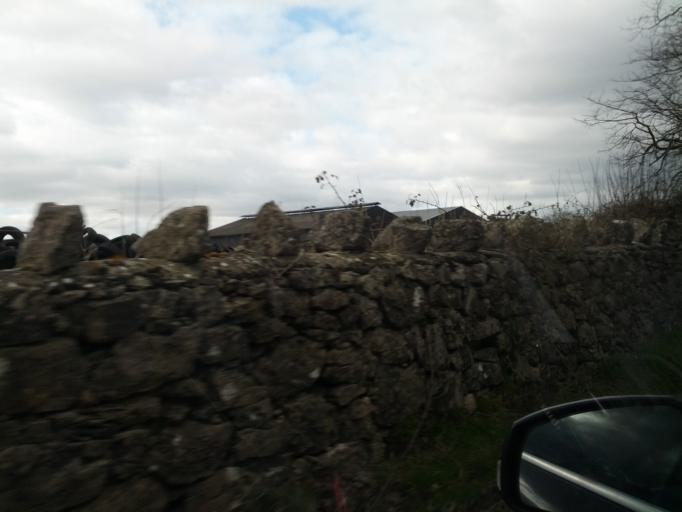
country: IE
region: Connaught
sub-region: County Galway
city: Athenry
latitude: 53.3881
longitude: -8.6609
